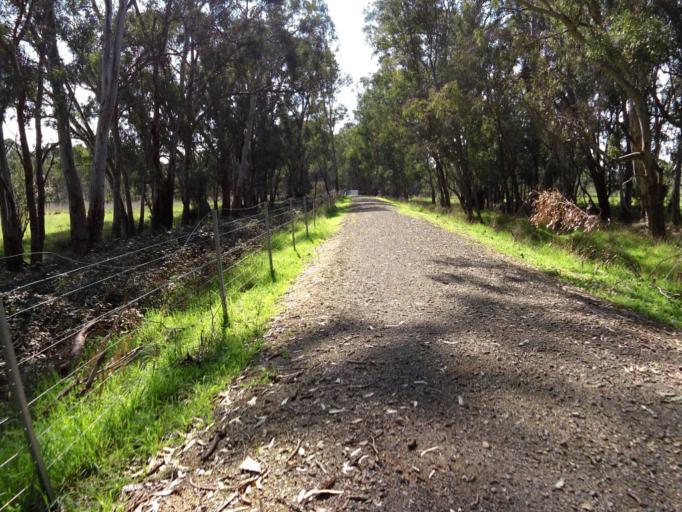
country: AU
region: Victoria
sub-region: Murrindindi
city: Alexandra
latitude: -37.1558
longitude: 145.5740
